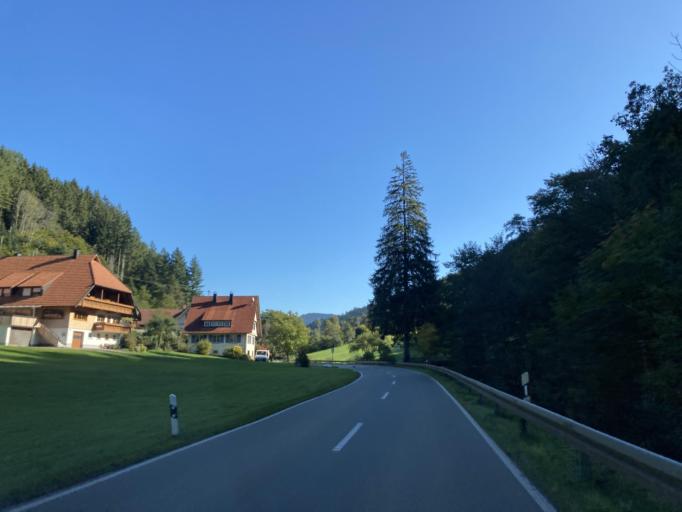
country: DE
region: Baden-Wuerttemberg
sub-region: Freiburg Region
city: Oberwolfach
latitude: 48.3538
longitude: 8.2525
